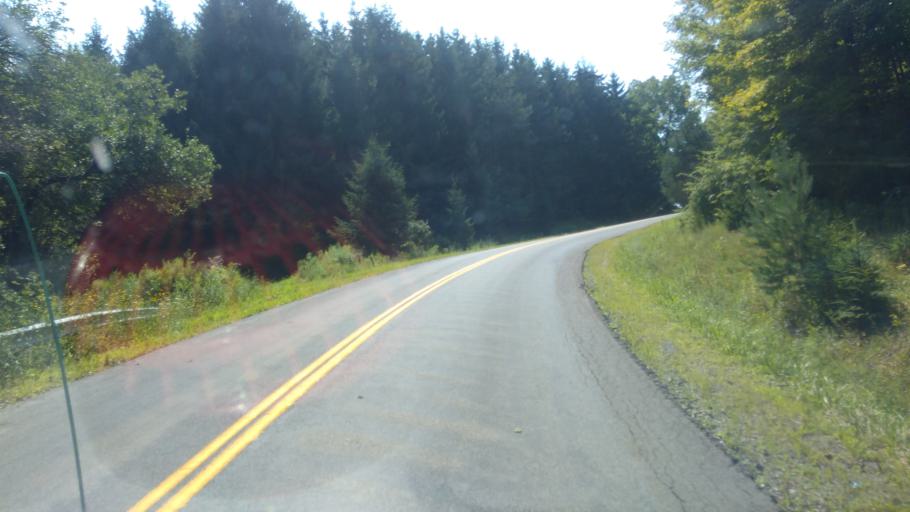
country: US
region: New York
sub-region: Steuben County
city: Canisteo
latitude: 42.3532
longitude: -77.5490
